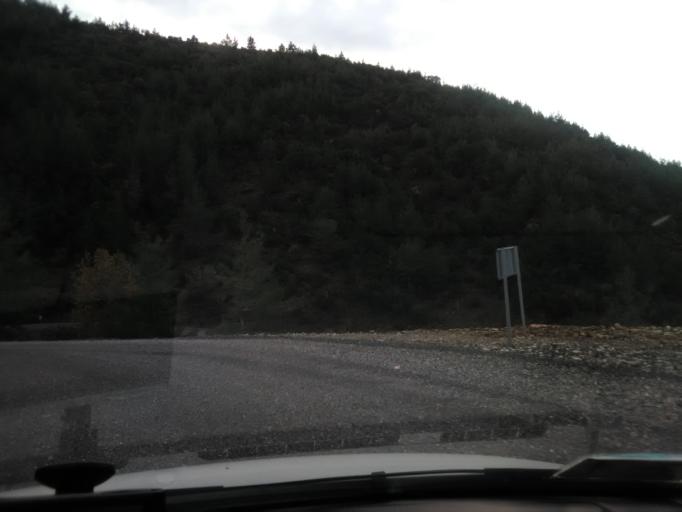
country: TR
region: Antalya
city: Gazipasa
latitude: 36.3034
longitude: 32.3910
